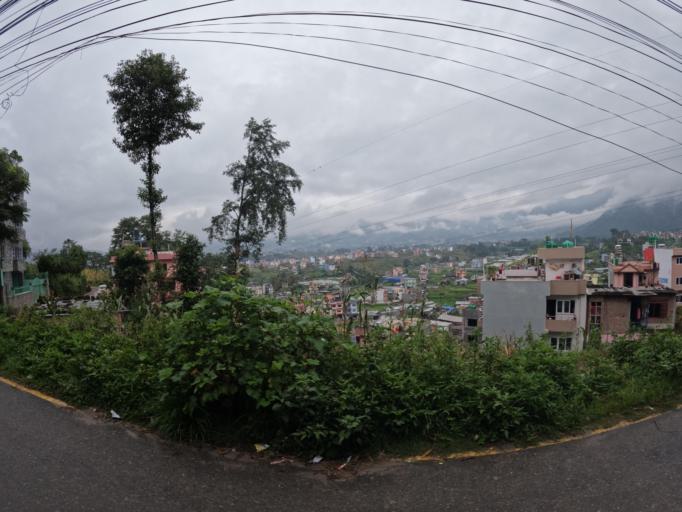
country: NP
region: Central Region
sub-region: Bagmati Zone
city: Kathmandu
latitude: 27.7617
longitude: 85.3245
